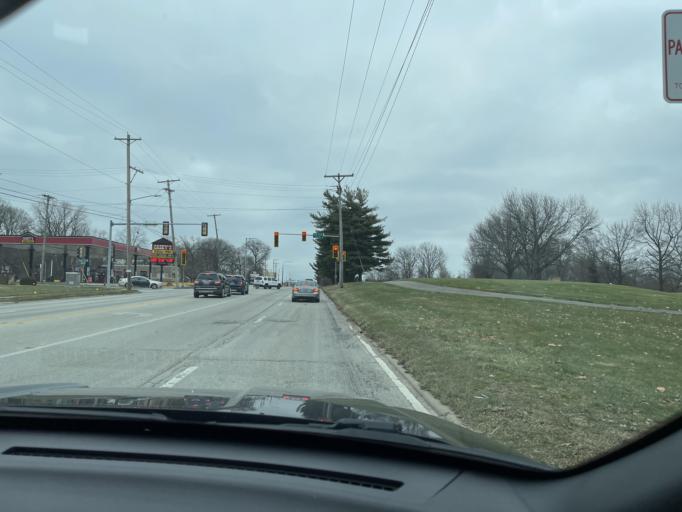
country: US
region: Illinois
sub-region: Sangamon County
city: Grandview
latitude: 39.8019
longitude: -89.6115
